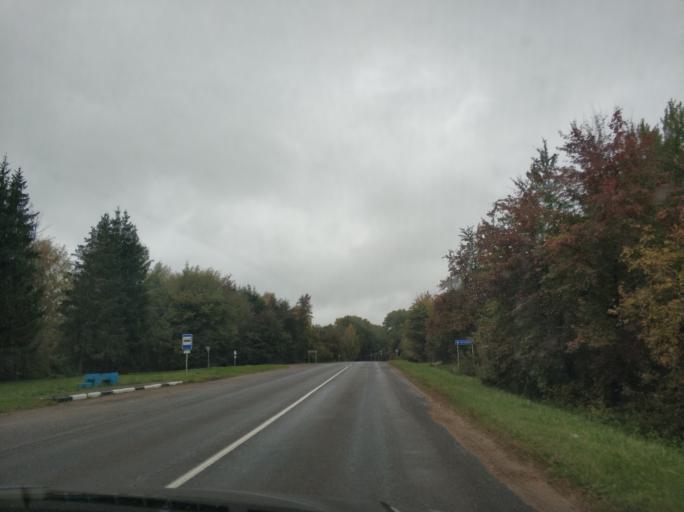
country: BY
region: Vitebsk
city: Polatsk
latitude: 55.4441
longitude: 28.9461
